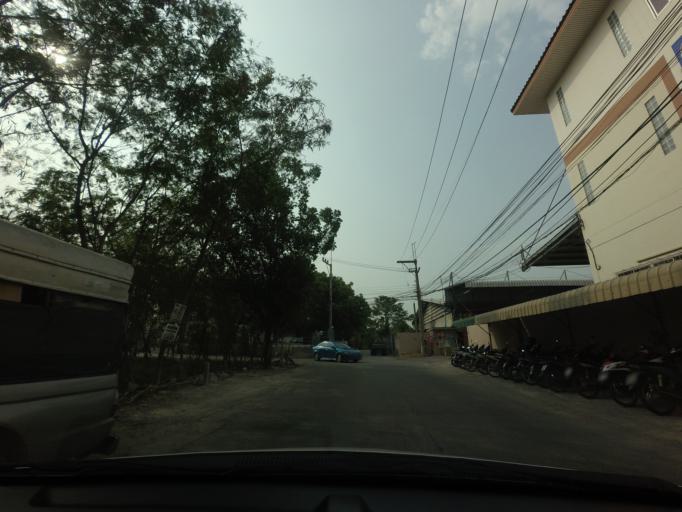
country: TH
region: Bangkok
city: Nong Khaem
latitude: 13.7335
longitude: 100.3344
